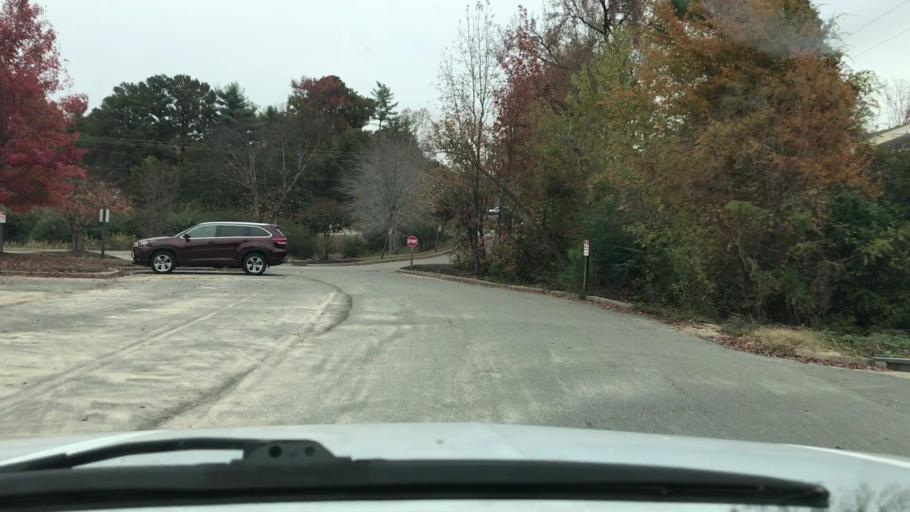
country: US
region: Virginia
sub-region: Henrico County
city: Tuckahoe
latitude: 37.5944
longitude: -77.5798
